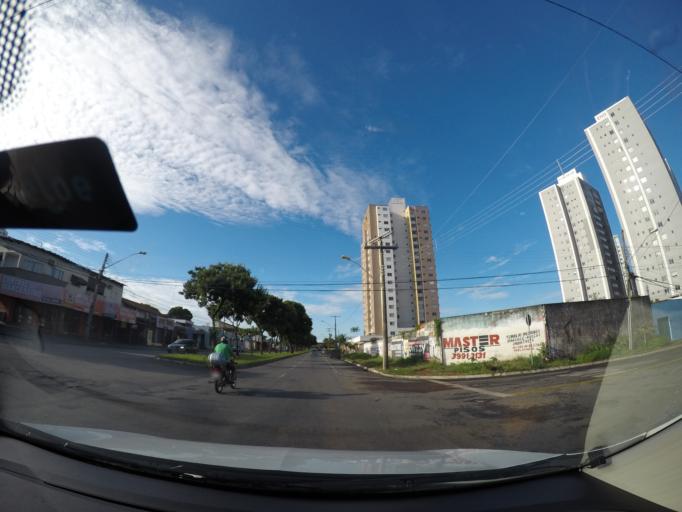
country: BR
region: Goias
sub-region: Goiania
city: Goiania
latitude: -16.7348
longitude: -49.2727
